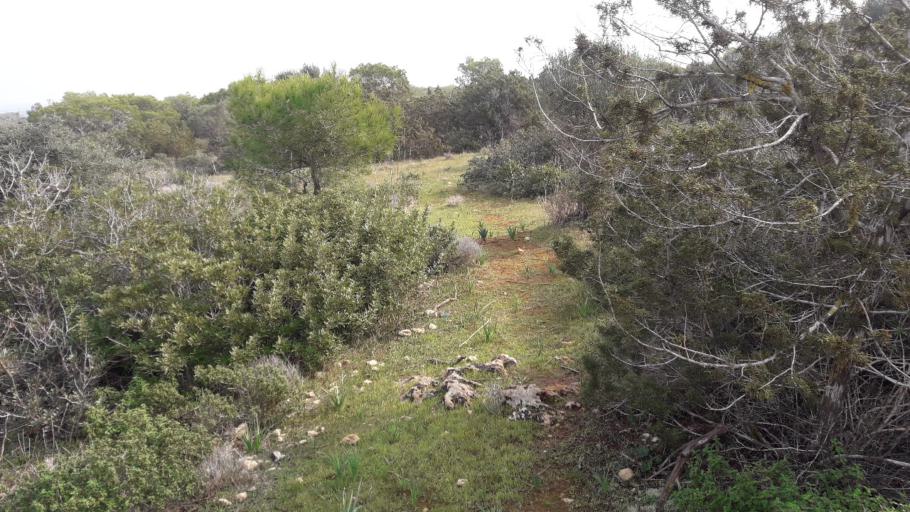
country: CY
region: Ammochostos
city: Leonarisso
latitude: 35.5030
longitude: 34.1440
